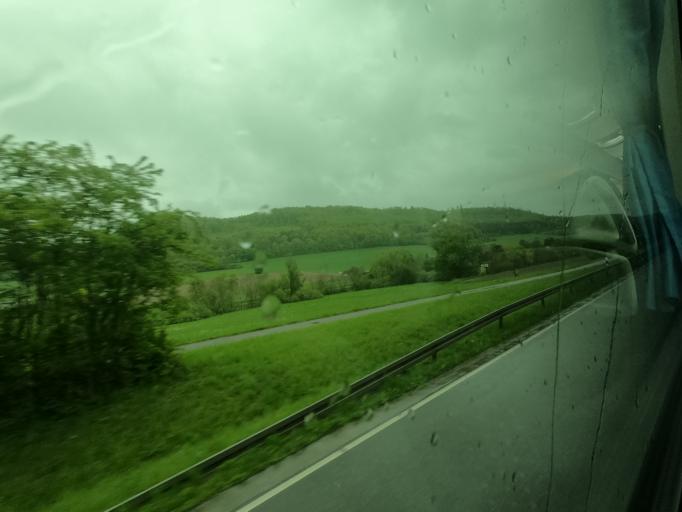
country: DE
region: Baden-Wuerttemberg
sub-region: Regierungsbezirk Stuttgart
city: Oberkochen
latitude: 48.8018
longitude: 10.1256
